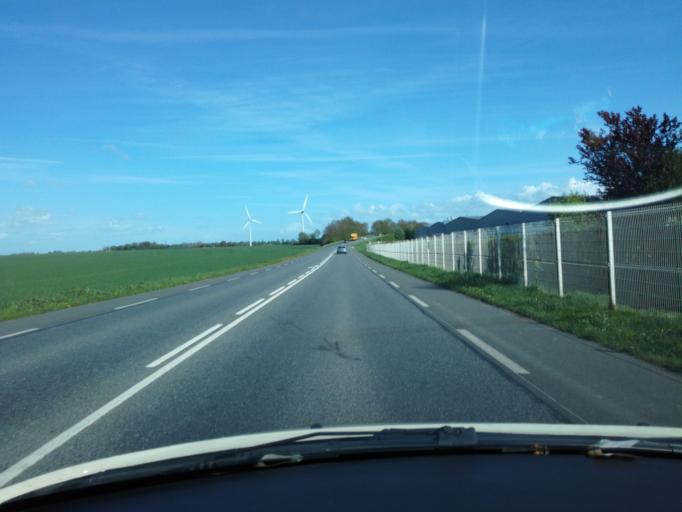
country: FR
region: Picardie
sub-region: Departement de la Somme
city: Feuquieres-en-Vimeu
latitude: 50.0682
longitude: 1.6108
